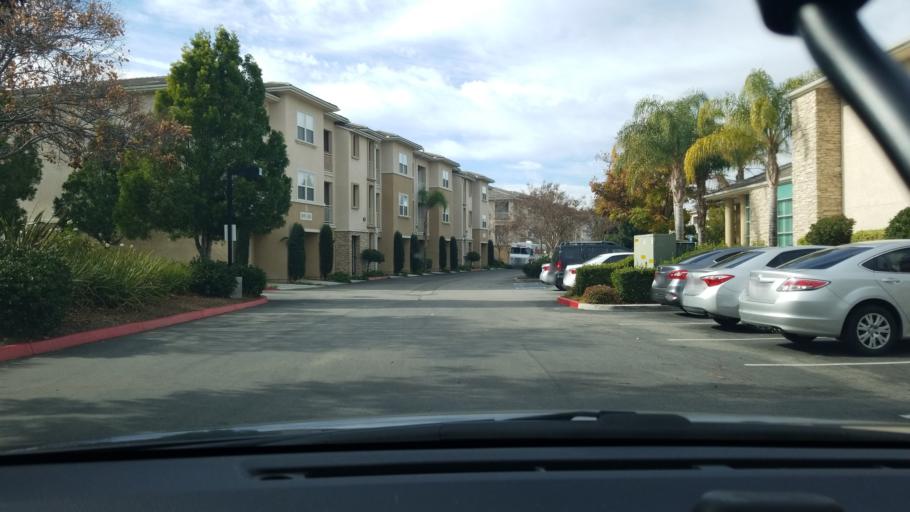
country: US
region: California
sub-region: Riverside County
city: Temecula
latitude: 33.4750
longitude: -117.1176
